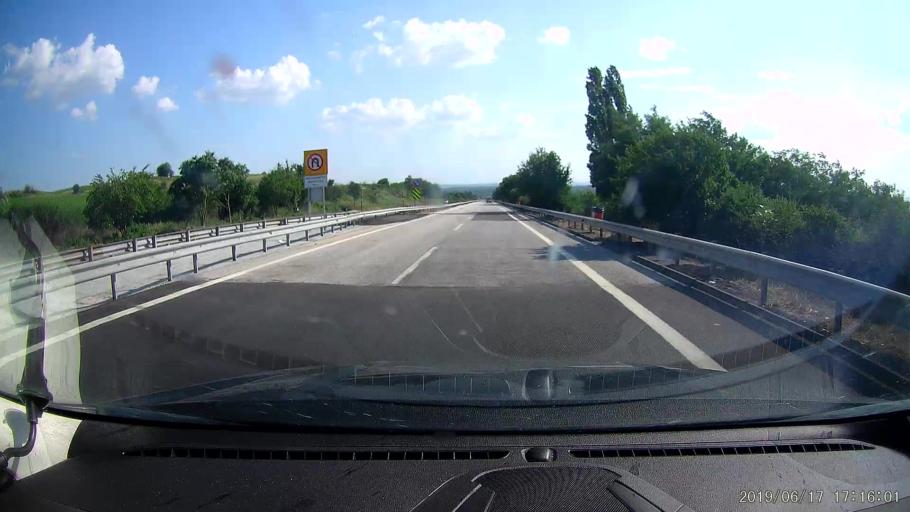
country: GR
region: East Macedonia and Thrace
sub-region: Nomos Evrou
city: Kastanies
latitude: 41.6976
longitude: 26.4863
